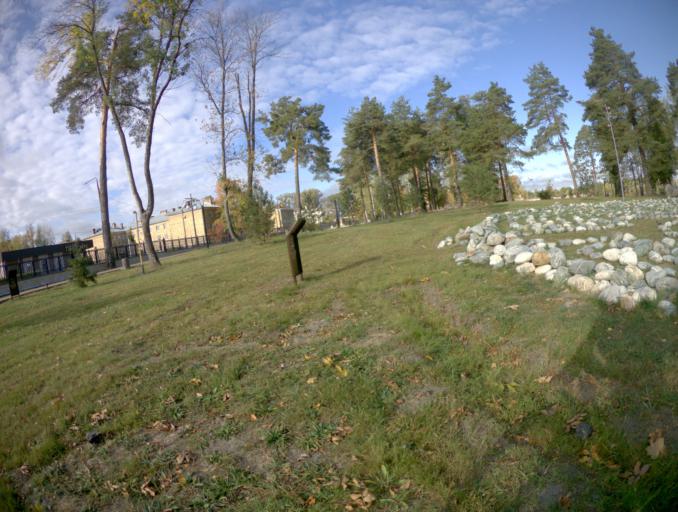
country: RU
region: Moskovskaya
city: Roshal'
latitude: 55.6596
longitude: 39.8674
